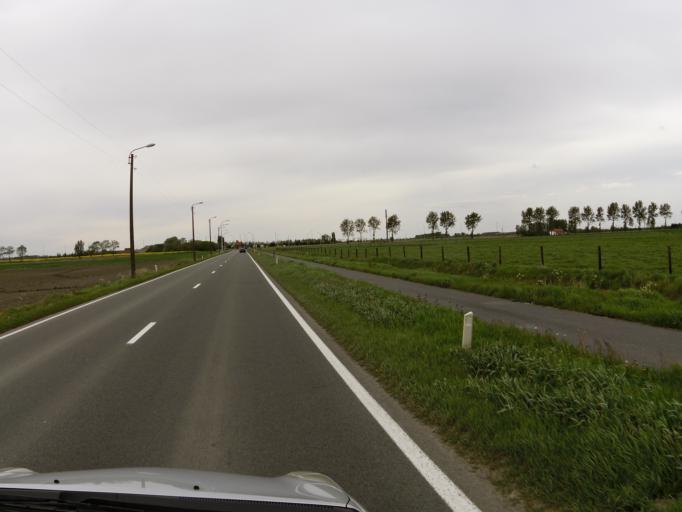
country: BE
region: Flanders
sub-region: Provincie West-Vlaanderen
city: Middelkerke
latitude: 51.1357
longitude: 2.8665
